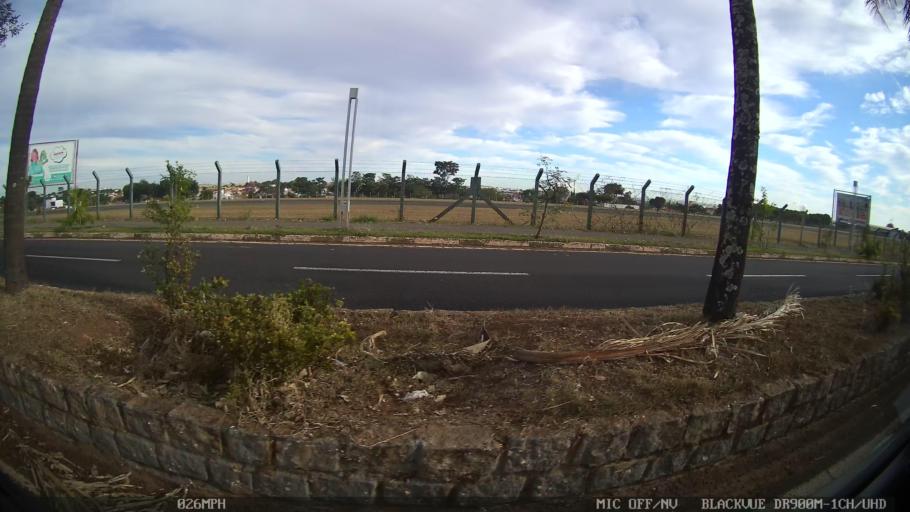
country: BR
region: Sao Paulo
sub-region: Catanduva
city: Catanduva
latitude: -21.1495
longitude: -48.9878
